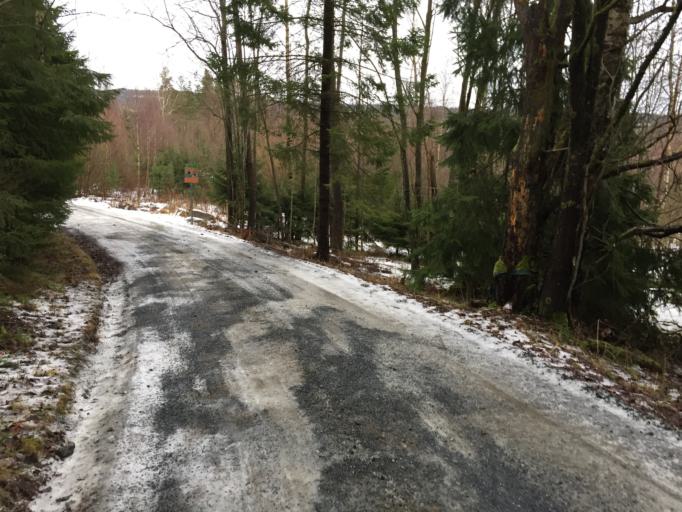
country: NO
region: Ostfold
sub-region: Moss
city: Moss
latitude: 59.4884
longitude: 10.6692
